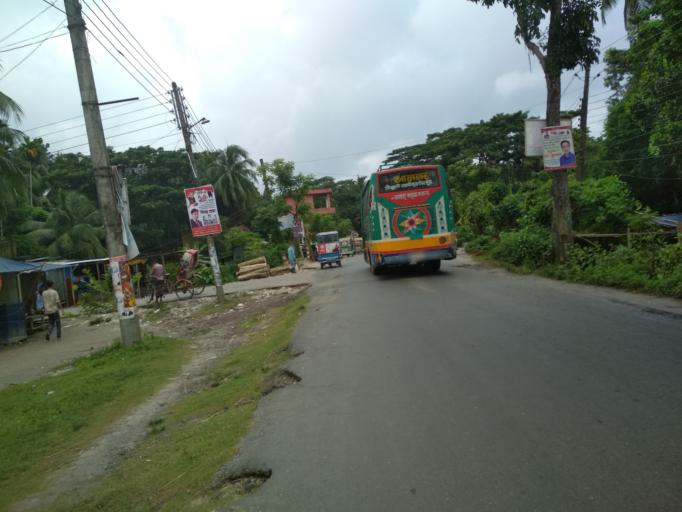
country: BD
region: Chittagong
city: Lakshmipur
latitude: 22.9466
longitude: 90.8094
